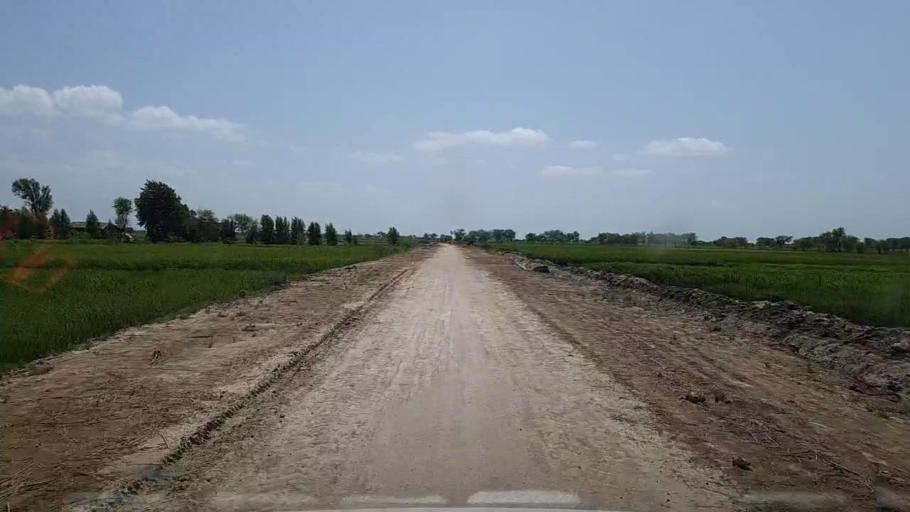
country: PK
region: Sindh
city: Kario
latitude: 24.6868
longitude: 68.5940
